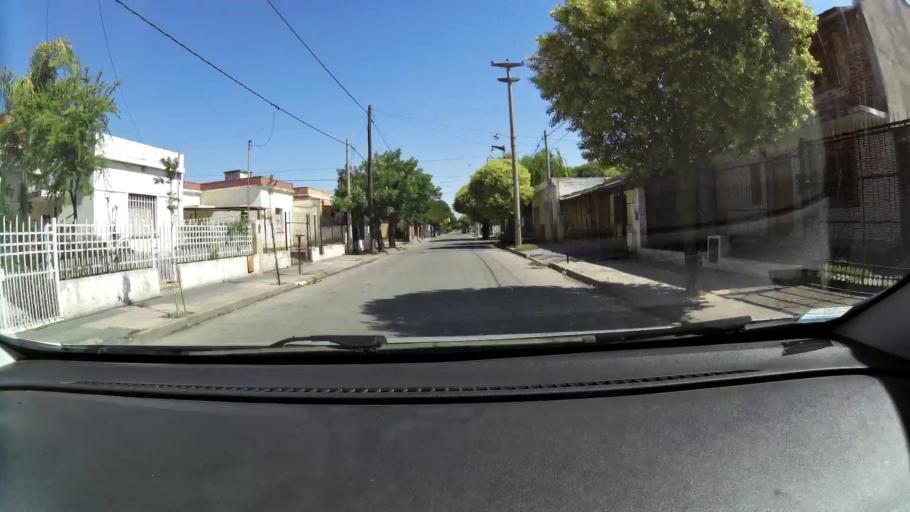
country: AR
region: Cordoba
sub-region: Departamento de Capital
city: Cordoba
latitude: -31.3711
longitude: -64.1366
